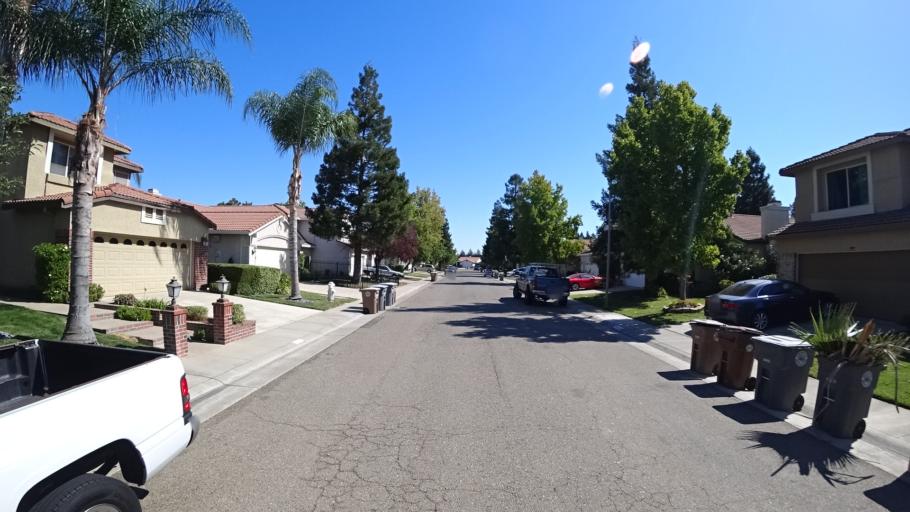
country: US
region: California
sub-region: Sacramento County
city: Laguna
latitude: 38.4240
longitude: -121.4231
